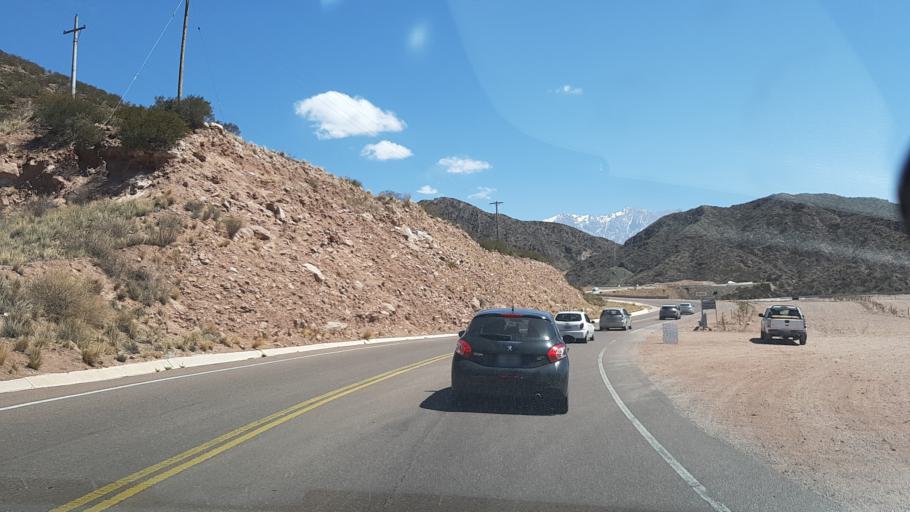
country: AR
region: Mendoza
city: Lujan de Cuyo
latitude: -32.9958
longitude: -69.1436
